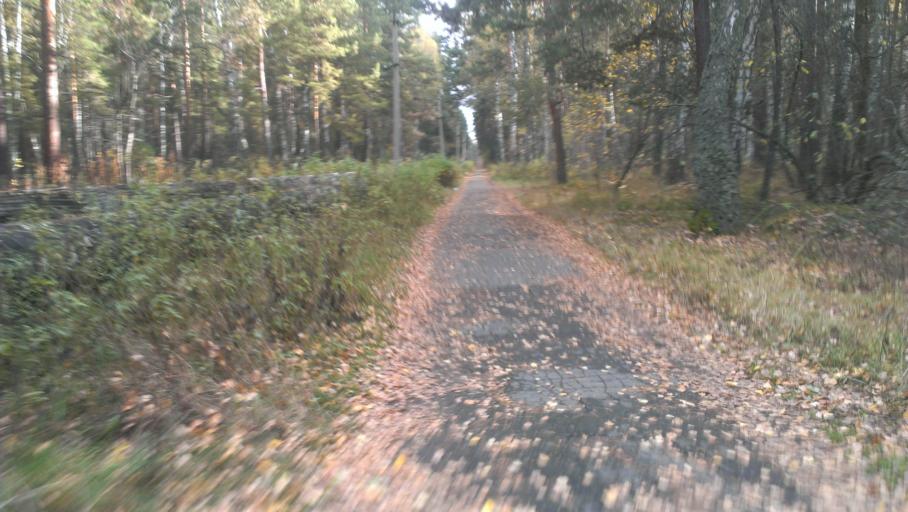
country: RU
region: Altai Krai
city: Yuzhnyy
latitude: 53.2696
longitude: 83.6815
